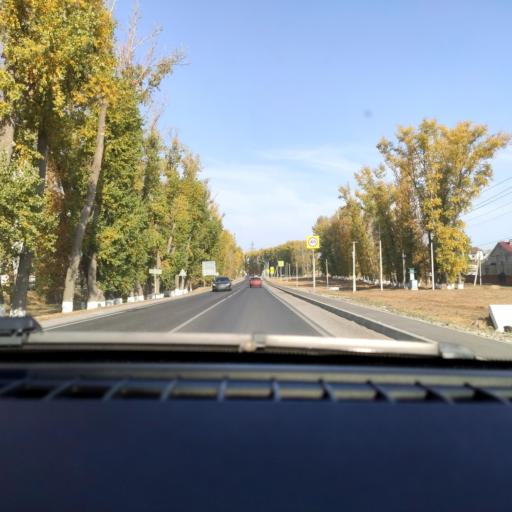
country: RU
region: Voronezj
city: Novaya Usman'
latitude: 51.6702
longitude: 39.4059
